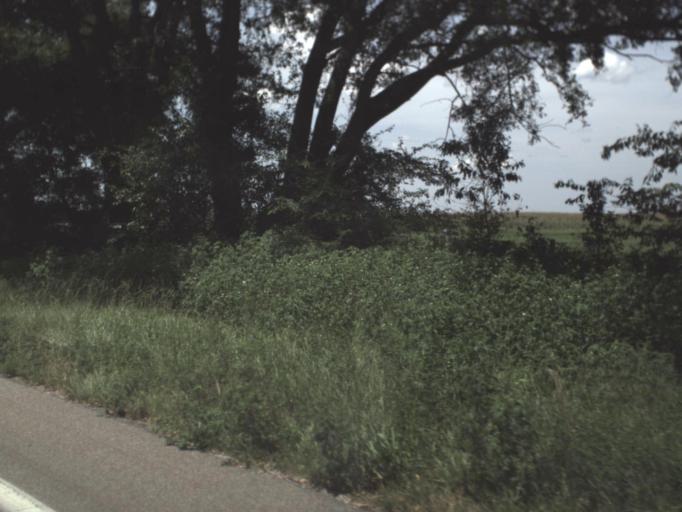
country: US
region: Florida
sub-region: Gilchrist County
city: Trenton
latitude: 29.6676
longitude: -82.8511
